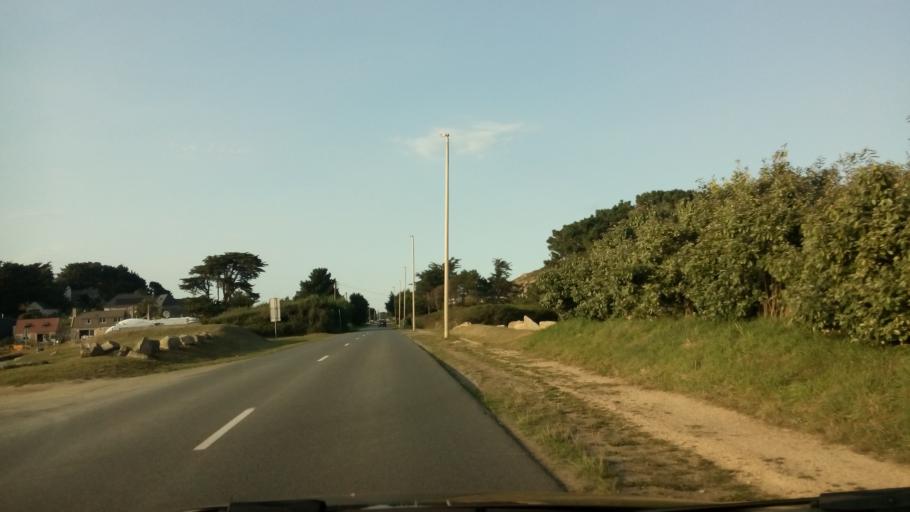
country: FR
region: Brittany
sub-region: Departement des Cotes-d'Armor
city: Trebeurden
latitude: 48.7832
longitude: -3.5778
